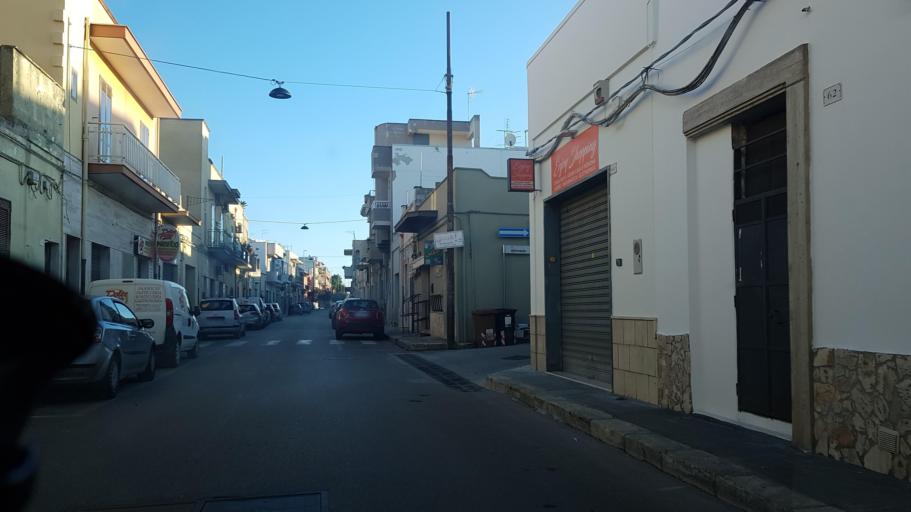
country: IT
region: Apulia
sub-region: Provincia di Brindisi
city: Latiano
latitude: 40.5503
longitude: 17.7180
